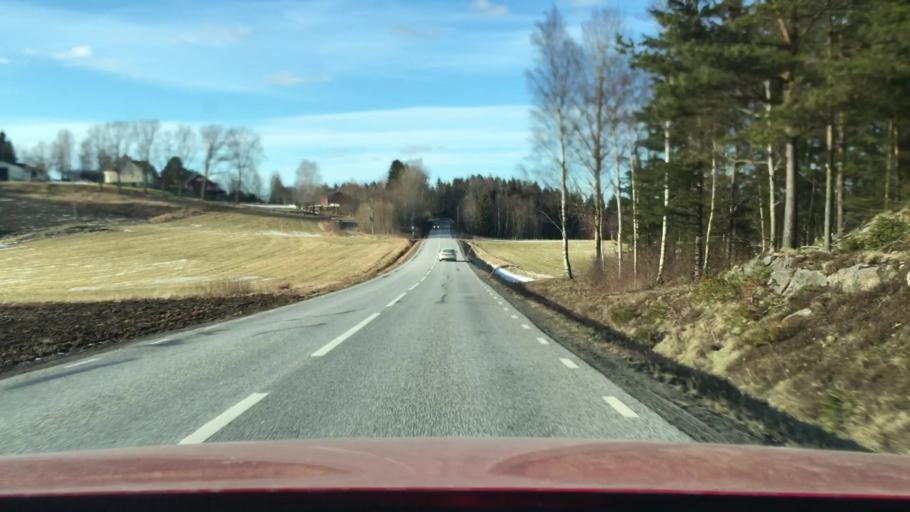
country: SE
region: Vaestra Goetaland
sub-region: Tanums Kommun
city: Tanumshede
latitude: 58.8063
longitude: 11.5531
